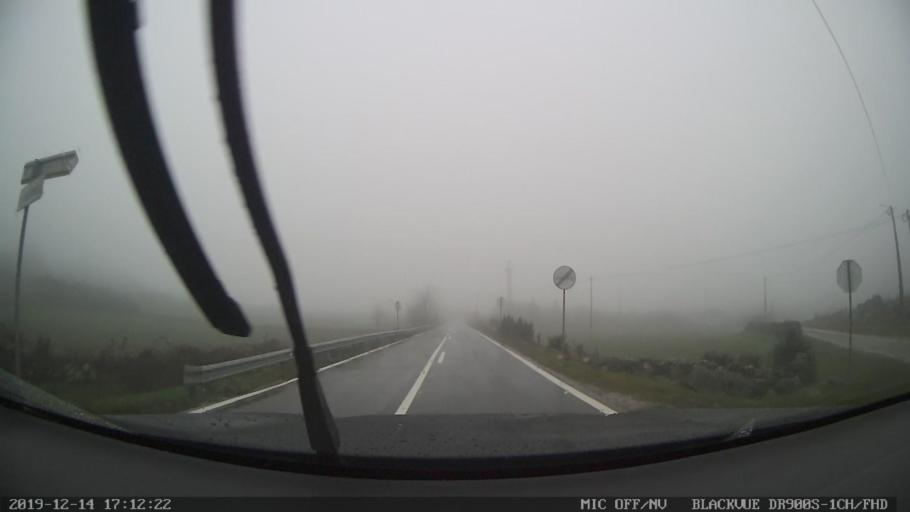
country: PT
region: Vila Real
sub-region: Vila Pouca de Aguiar
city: Vila Pouca de Aguiar
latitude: 41.4927
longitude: -7.6214
